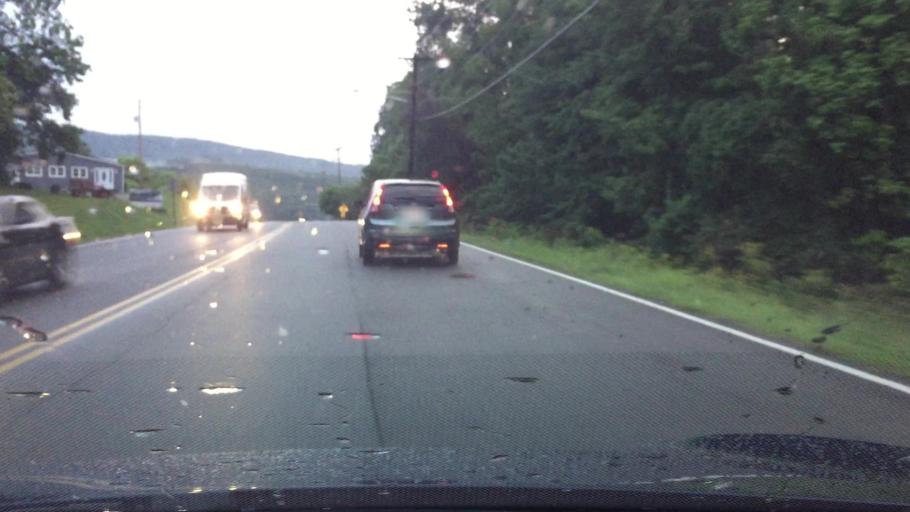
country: US
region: Virginia
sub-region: Pulaski County
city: Pulaski
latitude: 37.0501
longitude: -80.7532
